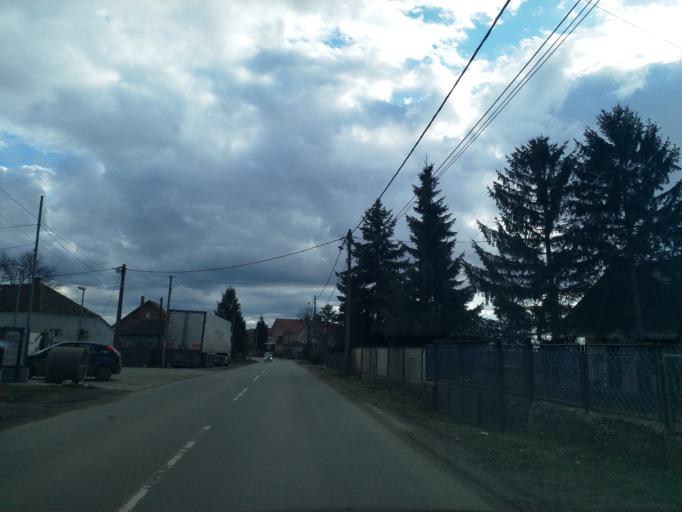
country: RS
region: Central Serbia
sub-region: Belgrade
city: Grocka
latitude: 44.6119
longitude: 20.7239
